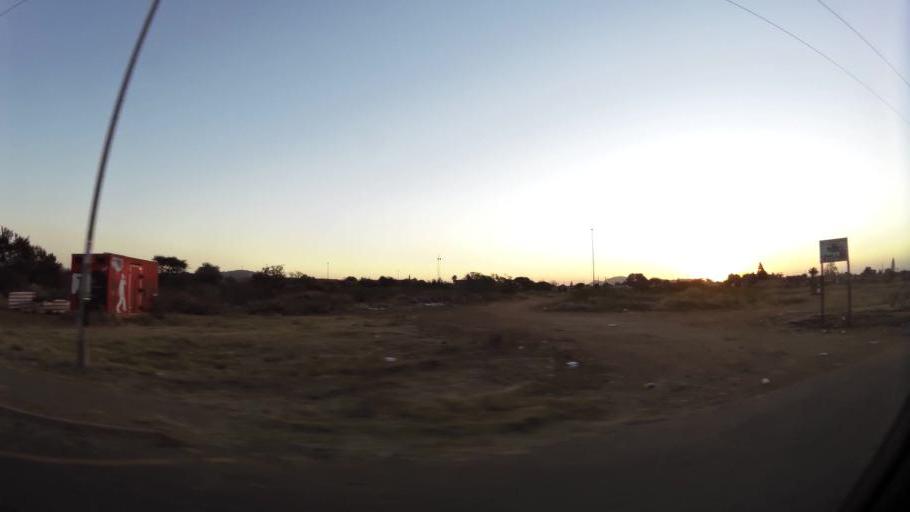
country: ZA
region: North-West
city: Ga-Rankuwa
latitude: -25.6152
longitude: 28.0069
